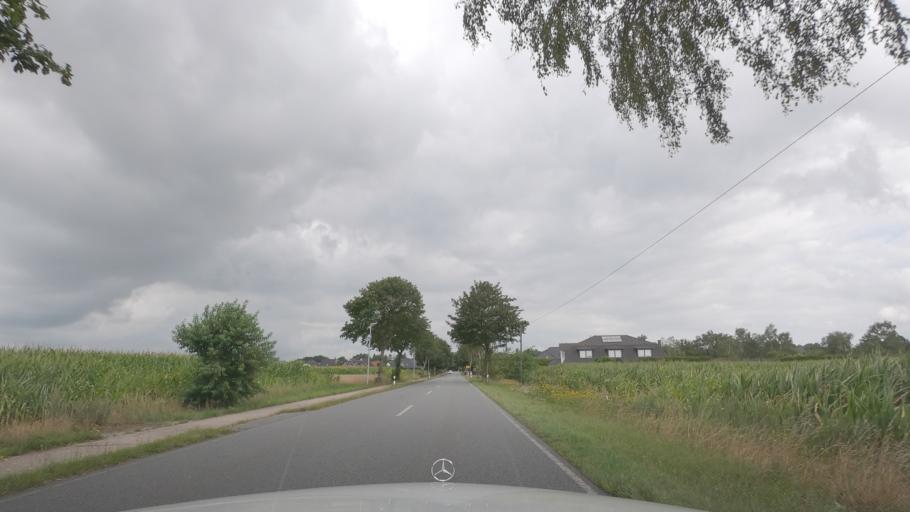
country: DE
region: Lower Saxony
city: Neuenkirchen
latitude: 53.2267
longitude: 8.5317
